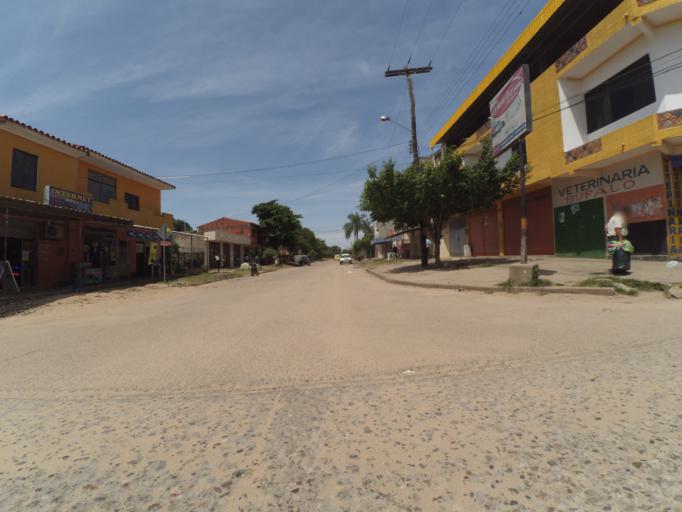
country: BO
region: Santa Cruz
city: Santa Cruz de la Sierra
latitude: -17.8256
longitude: -63.2288
